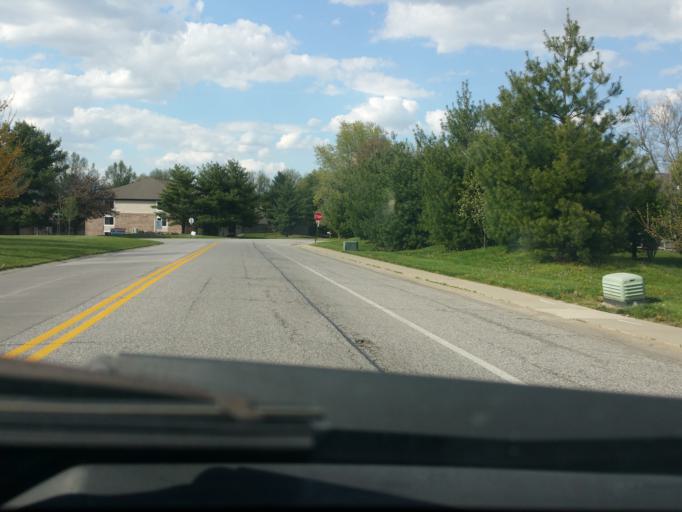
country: US
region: Illinois
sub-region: Madison County
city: Edwardsville
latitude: 38.7960
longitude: -89.9693
